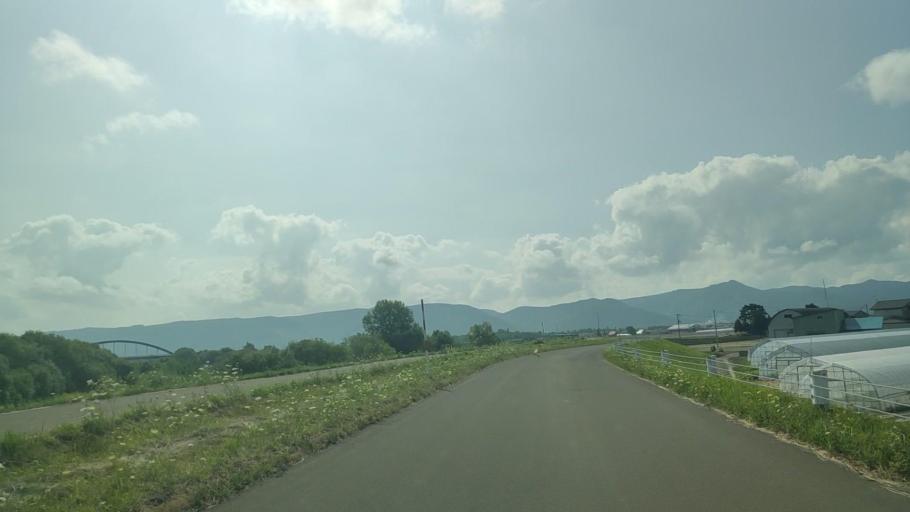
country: JP
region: Hokkaido
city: Shimo-furano
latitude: 43.3391
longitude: 142.3770
